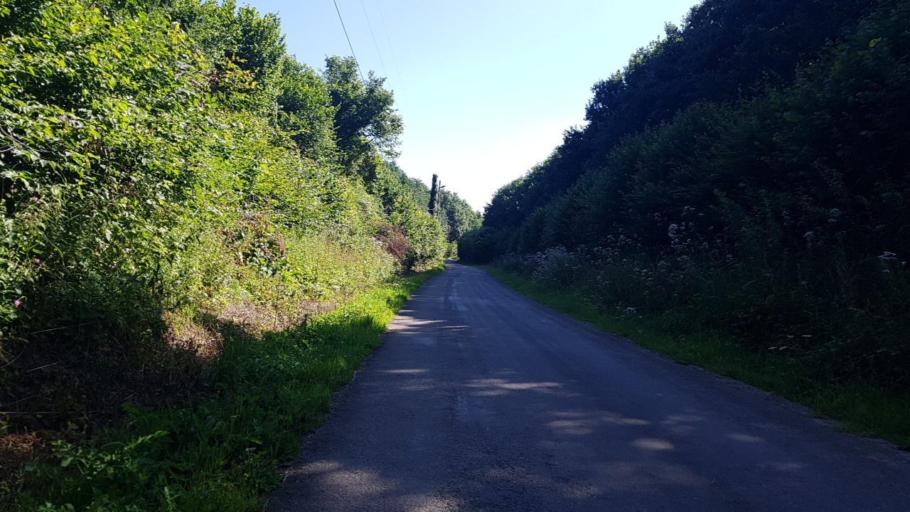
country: FR
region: Nord-Pas-de-Calais
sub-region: Departement du Nord
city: Anor
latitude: 49.9775
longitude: 4.1245
